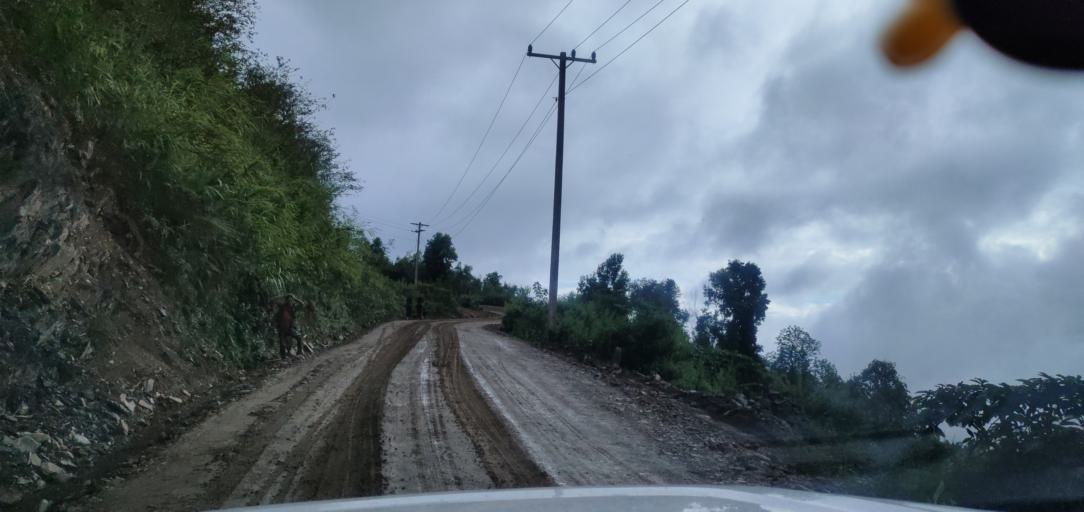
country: LA
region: Phongsali
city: Phongsali
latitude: 21.4231
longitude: 102.1712
